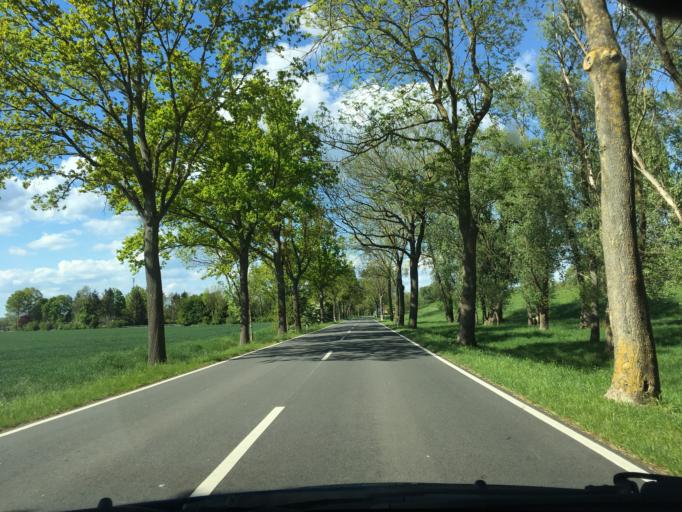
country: DE
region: Brandenburg
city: Lanz
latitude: 53.0303
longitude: 11.5606
